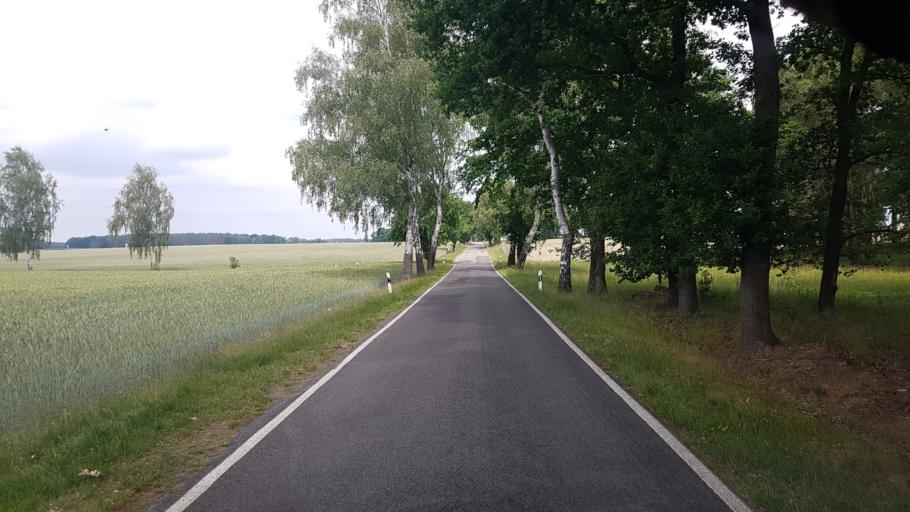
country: DE
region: Brandenburg
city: Lebusa
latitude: 51.8024
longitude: 13.4524
